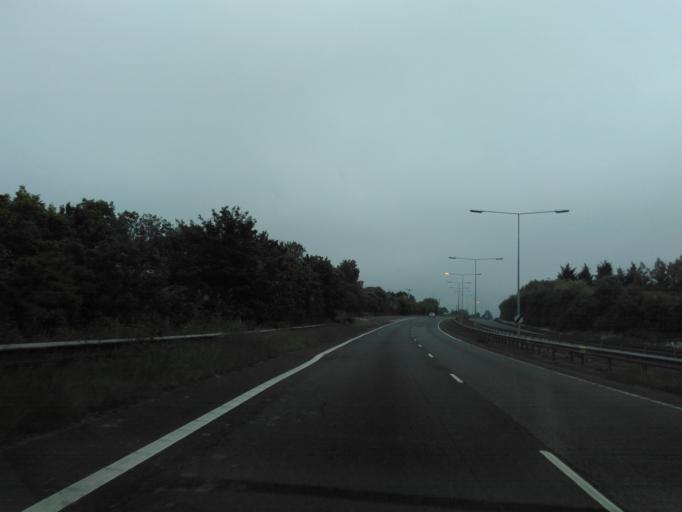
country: GB
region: England
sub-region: Kent
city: Whitstable
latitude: 51.3323
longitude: 0.9999
